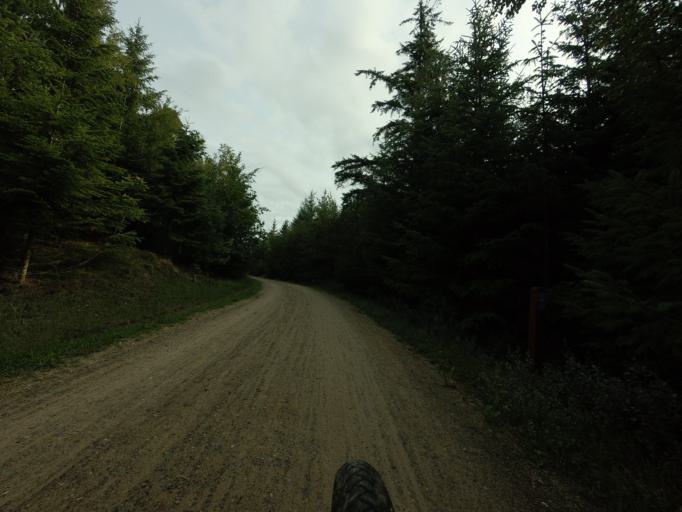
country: DK
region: North Denmark
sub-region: Hjorring Kommune
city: Sindal
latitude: 57.5855
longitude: 10.1119
